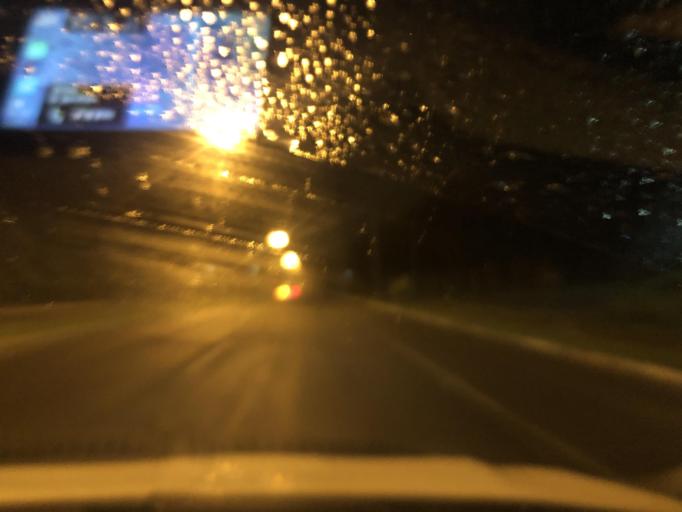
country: BR
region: Santa Catarina
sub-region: Joinville
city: Joinville
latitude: -26.3764
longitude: -48.8414
